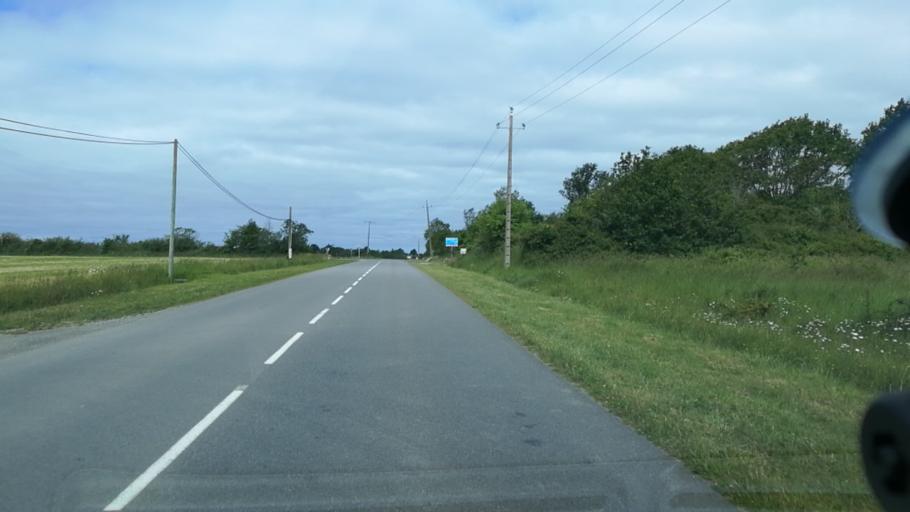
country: FR
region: Brittany
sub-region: Departement du Morbihan
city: Penestin
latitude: 47.4559
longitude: -2.4685
